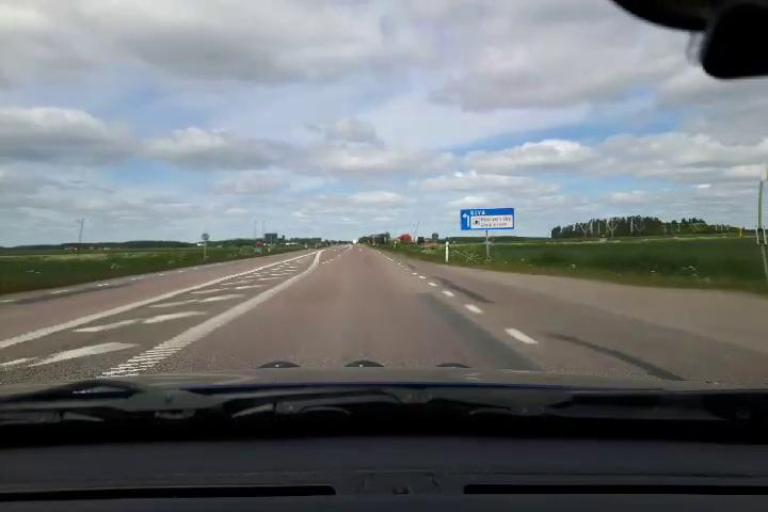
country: SE
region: Uppsala
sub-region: Uppsala Kommun
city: Gamla Uppsala
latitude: 59.9107
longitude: 17.6074
